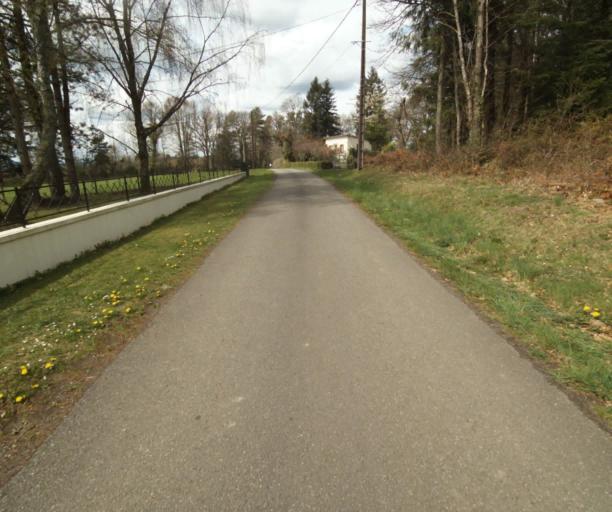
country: FR
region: Limousin
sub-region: Departement de la Correze
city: Laguenne
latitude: 45.2231
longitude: 1.8845
